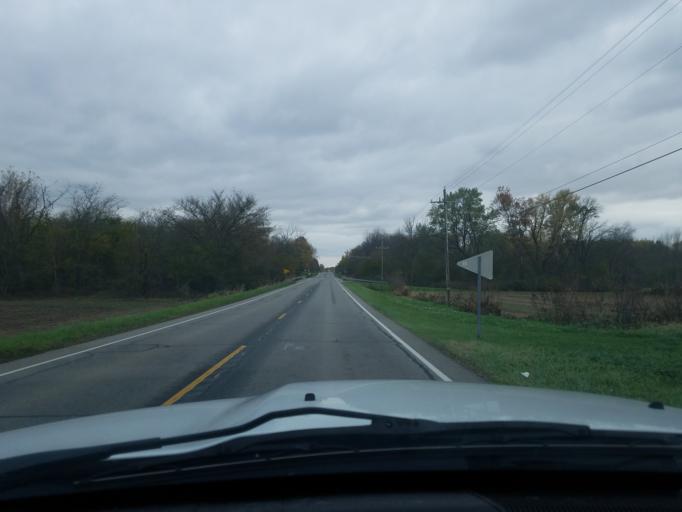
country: US
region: Indiana
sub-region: Bartholomew County
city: Hope
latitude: 39.3163
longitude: -85.7714
